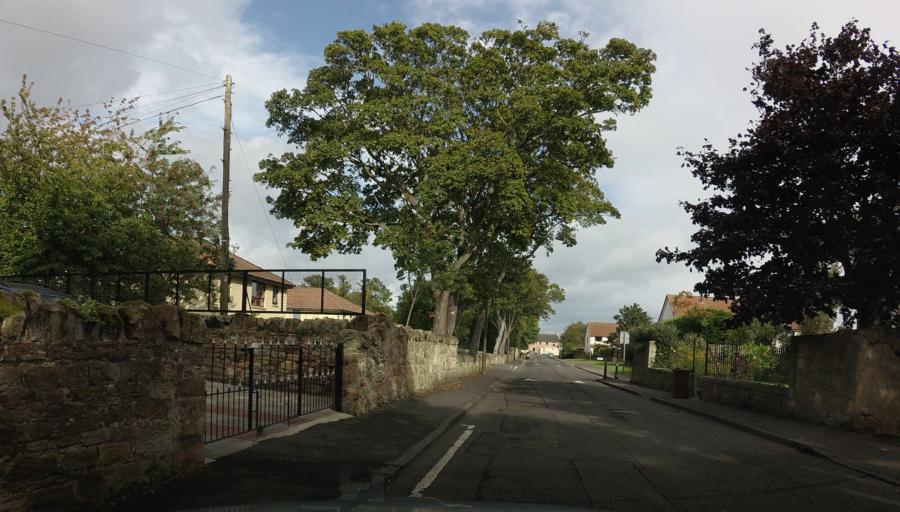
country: GB
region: Scotland
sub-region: East Lothian
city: Prestonpans
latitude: 55.9586
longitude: -2.9784
